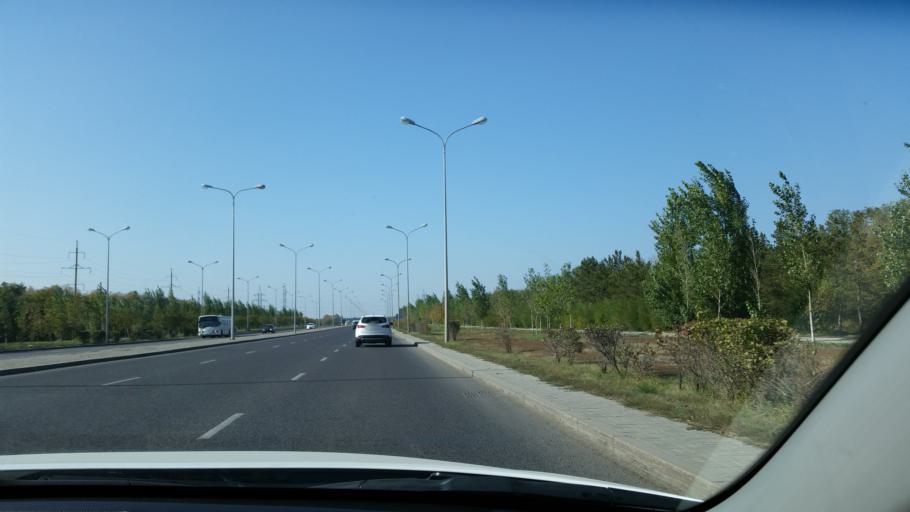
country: KZ
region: Astana Qalasy
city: Astana
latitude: 51.1961
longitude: 71.3169
